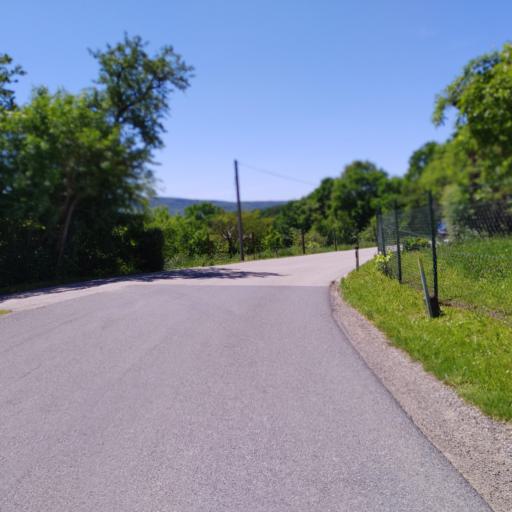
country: AT
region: Lower Austria
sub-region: Politischer Bezirk Sankt Polten
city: Maria-Anzbach
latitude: 48.2031
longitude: 15.9383
